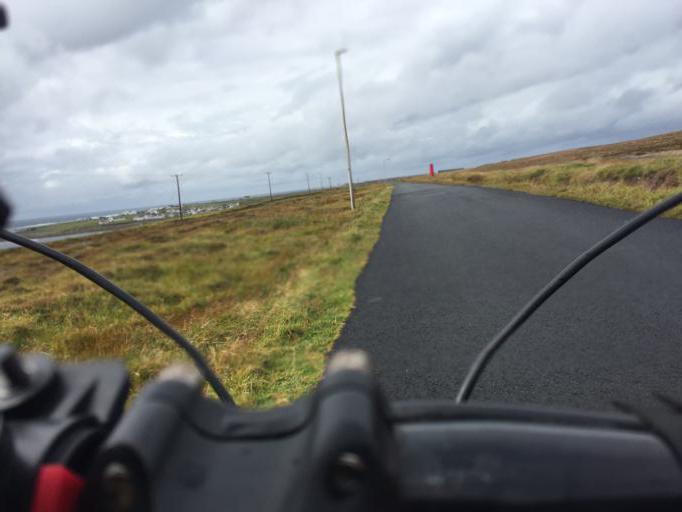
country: IE
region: Ulster
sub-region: County Donegal
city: Derrybeg
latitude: 55.2621
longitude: -8.2153
